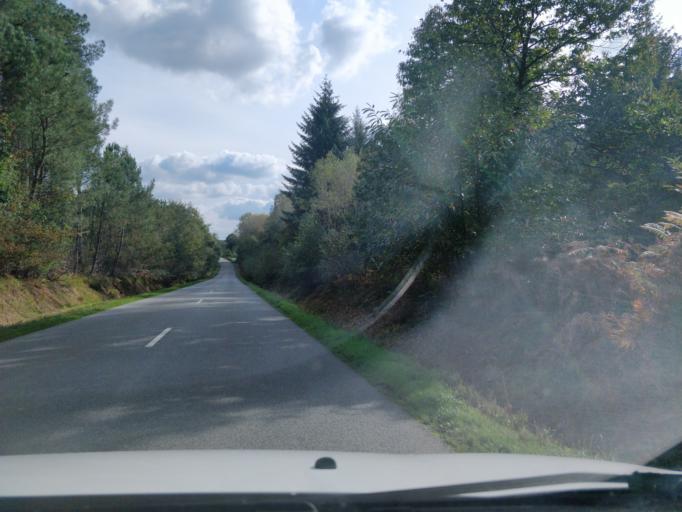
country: FR
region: Brittany
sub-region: Departement d'Ille-et-Vilaine
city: Chateaubourg
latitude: 48.1488
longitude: -1.4056
